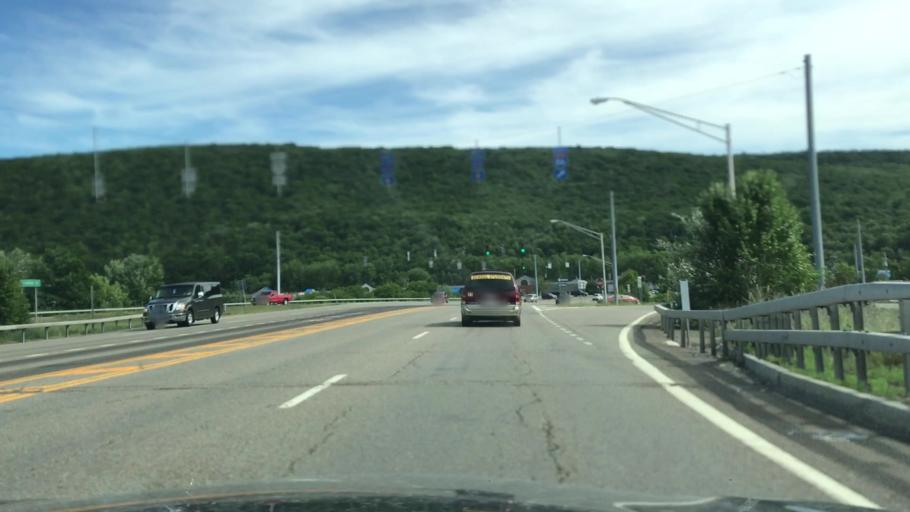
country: US
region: New York
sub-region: Chemung County
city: Horseheads
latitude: 42.1565
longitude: -76.8776
